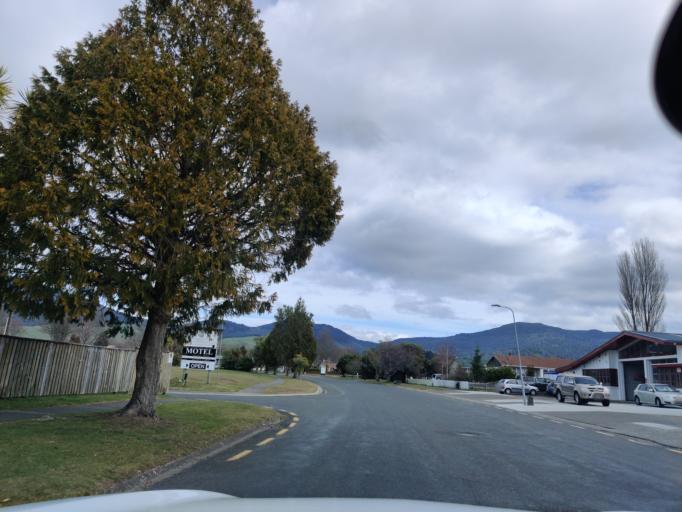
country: NZ
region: Waikato
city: Turangi
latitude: -38.9904
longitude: 175.8070
